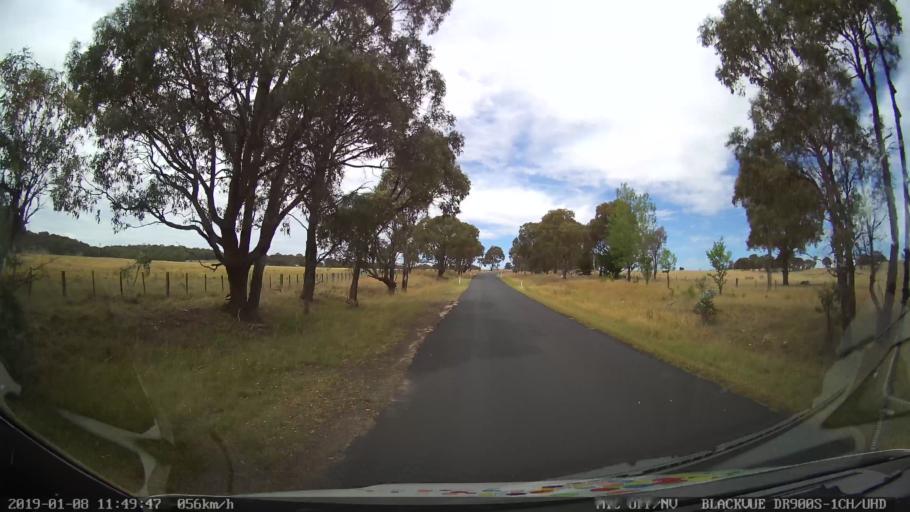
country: AU
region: New South Wales
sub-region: Armidale Dumaresq
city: Armidale
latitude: -30.3769
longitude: 151.5585
